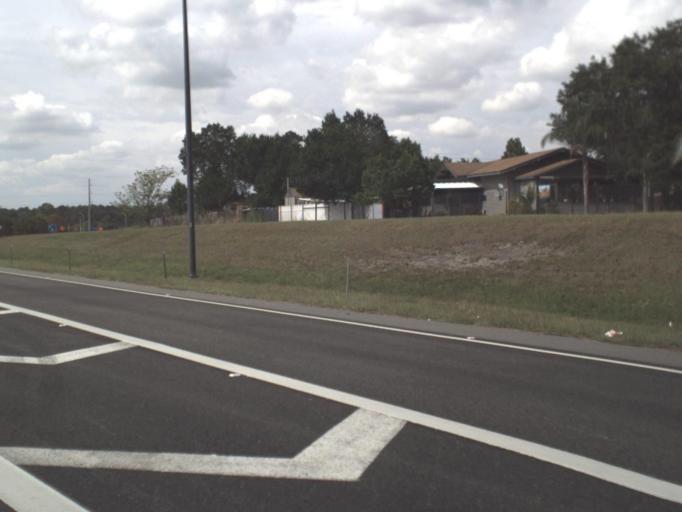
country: US
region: Florida
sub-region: Polk County
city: Crystal Lake
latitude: 28.0027
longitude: -81.8969
